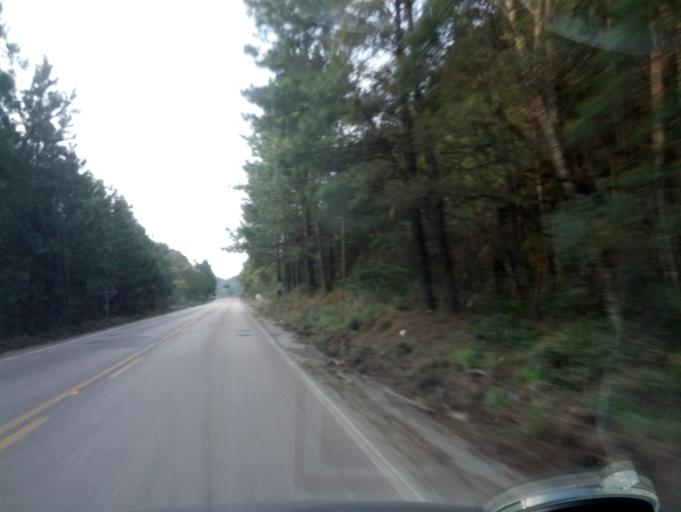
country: BR
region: Santa Catarina
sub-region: Otacilio Costa
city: Otacilio Costa
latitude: -27.3137
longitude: -50.1365
